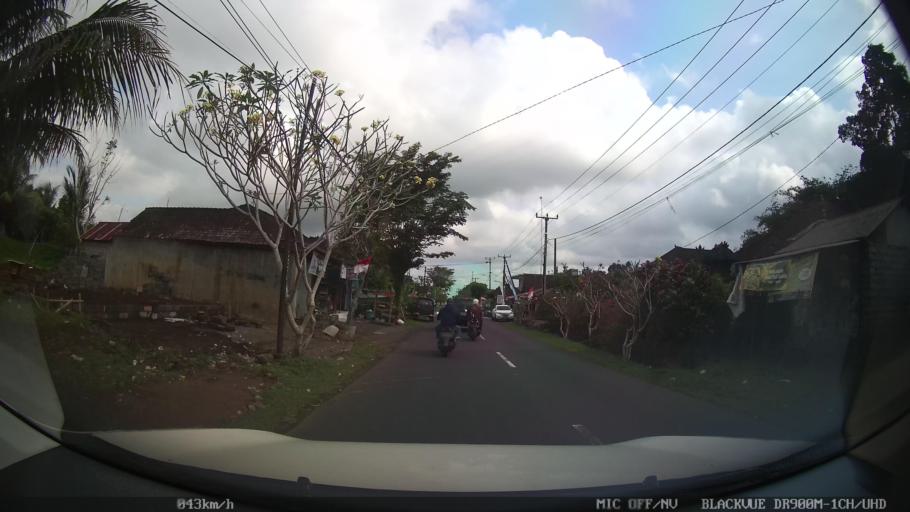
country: ID
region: Bali
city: Wanasari Baleran
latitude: -8.4735
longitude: 115.1368
